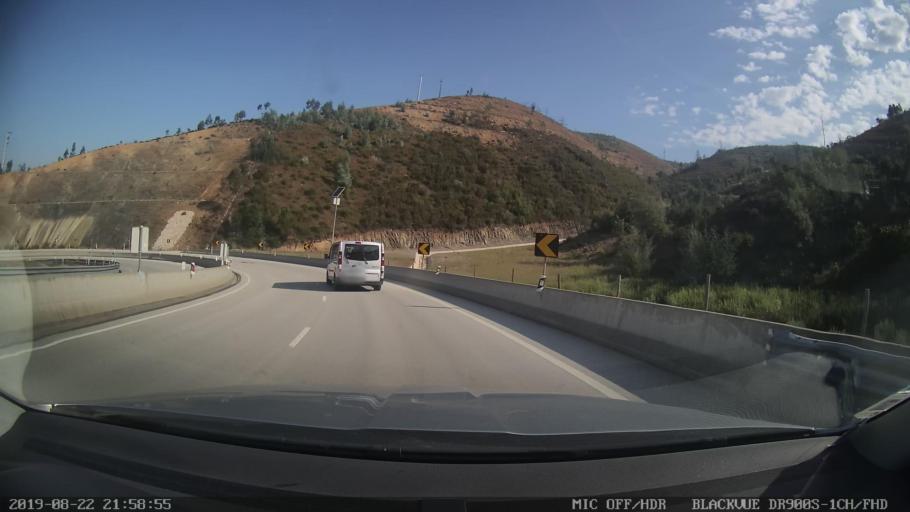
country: PT
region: Coimbra
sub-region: Coimbra
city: Coimbra
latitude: 40.1806
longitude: -8.3893
